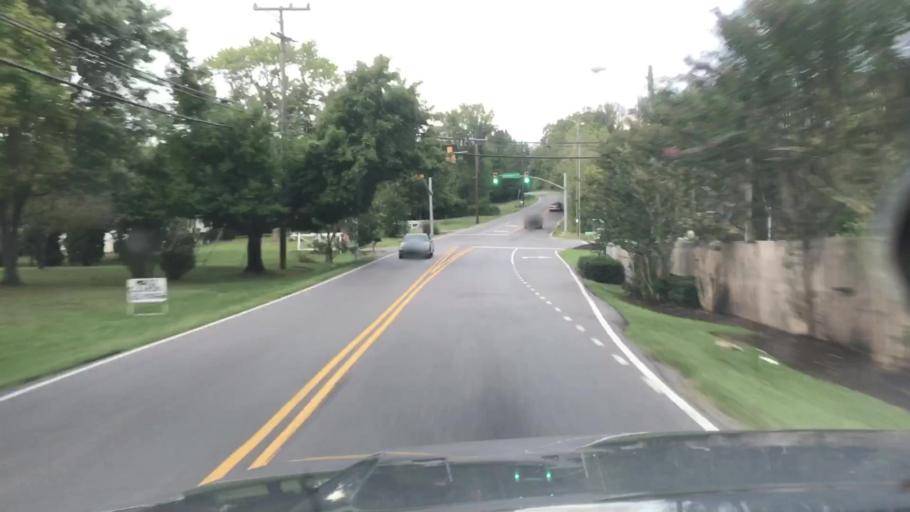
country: US
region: Tennessee
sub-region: Rutherford County
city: La Vergne
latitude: 36.0447
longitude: -86.6288
